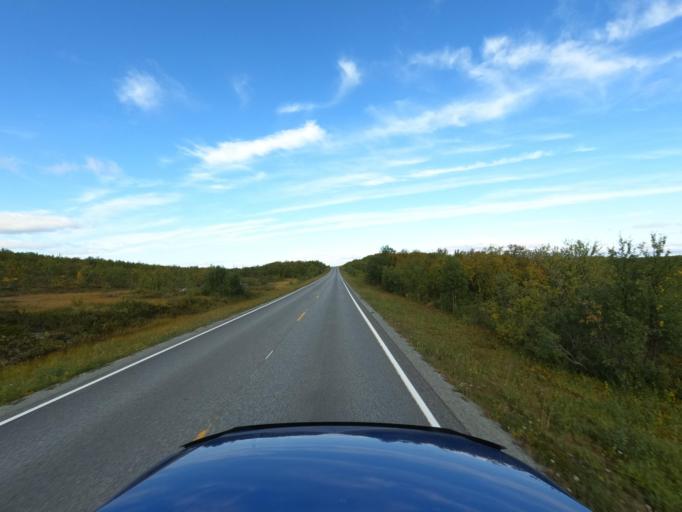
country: NO
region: Finnmark Fylke
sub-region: Karasjok
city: Karasjohka
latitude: 69.6914
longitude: 25.2594
